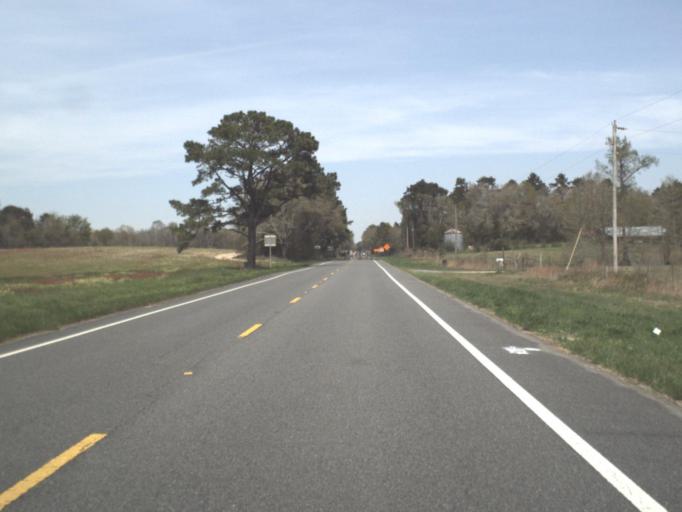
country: US
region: Alabama
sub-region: Geneva County
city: Samson
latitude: 30.9864
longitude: -85.9975
